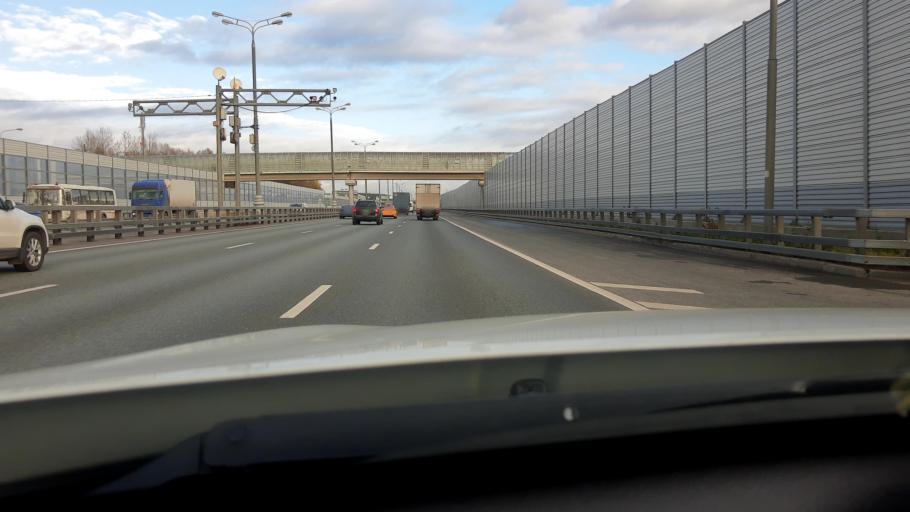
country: RU
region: Moskovskaya
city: Aprelevka
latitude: 55.5361
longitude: 37.0673
